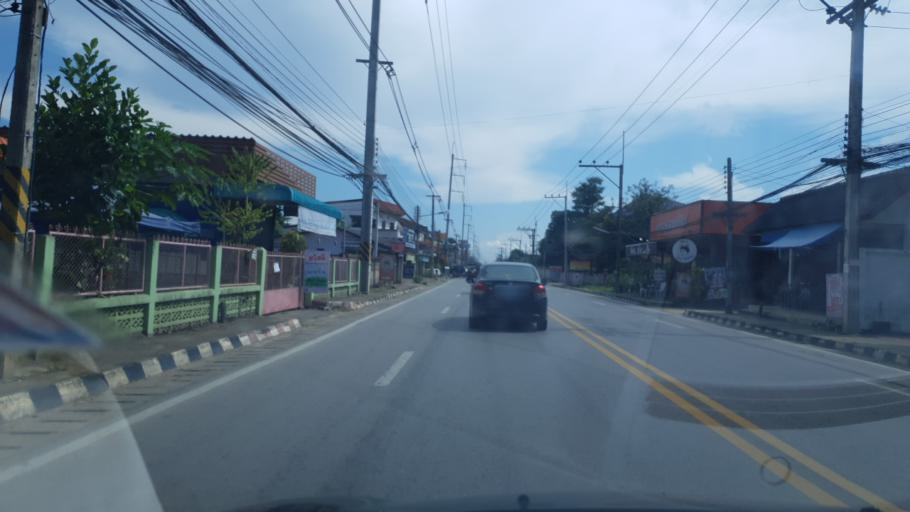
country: TH
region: Chiang Rai
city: Wiang Pa Pao
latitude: 19.3563
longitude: 99.5053
